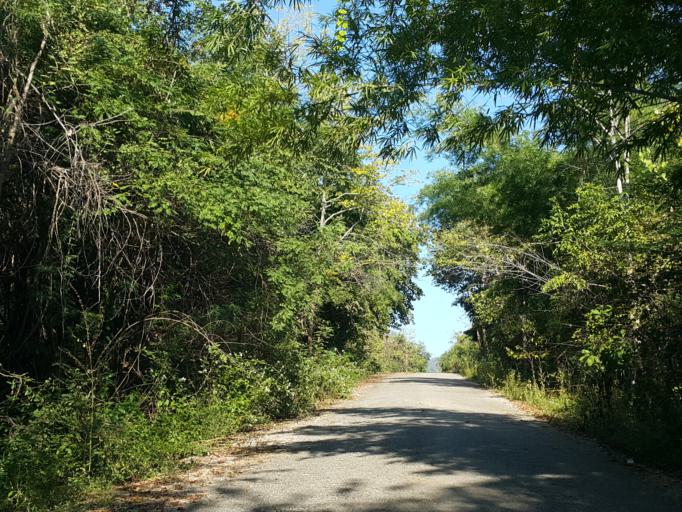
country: TH
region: Lampang
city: Mae Mo
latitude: 18.3007
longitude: 99.6653
